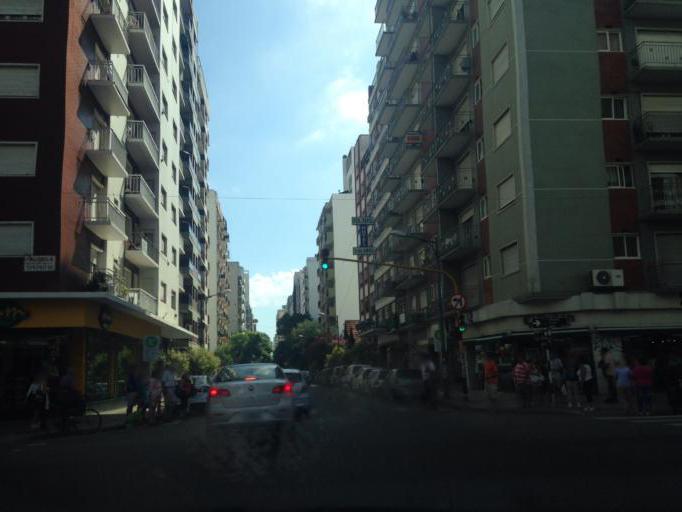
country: AR
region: Buenos Aires
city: Mar del Plata
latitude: -38.0036
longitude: -57.5502
